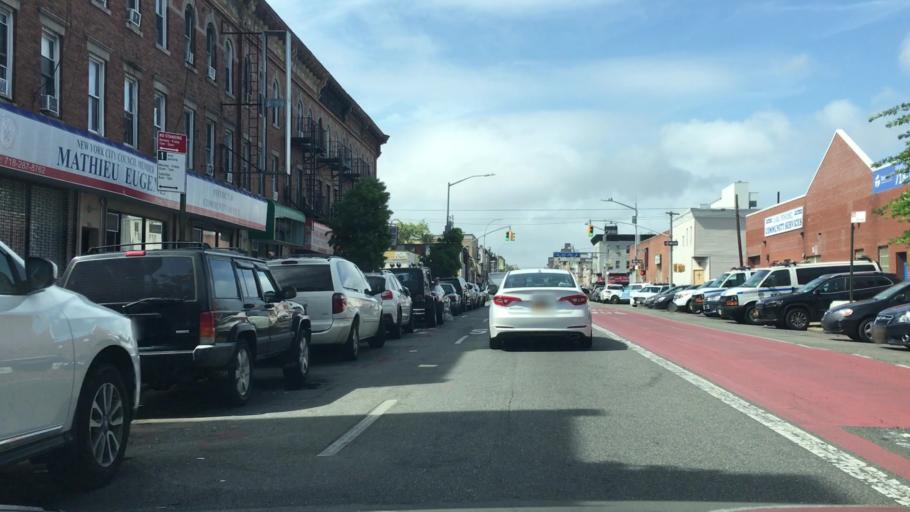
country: US
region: New York
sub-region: Kings County
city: Brooklyn
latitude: 40.6483
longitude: -73.9522
